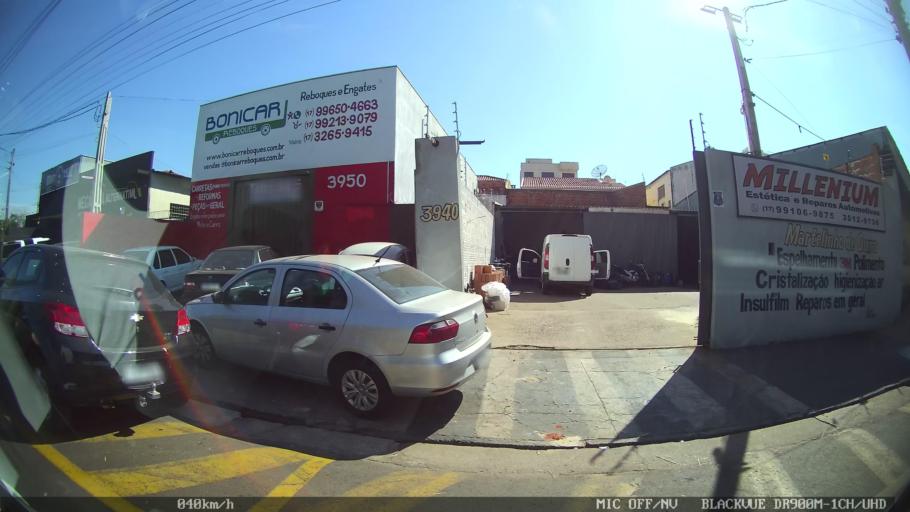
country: BR
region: Sao Paulo
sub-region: Sao Jose Do Rio Preto
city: Sao Jose do Rio Preto
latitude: -20.8025
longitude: -49.4090
